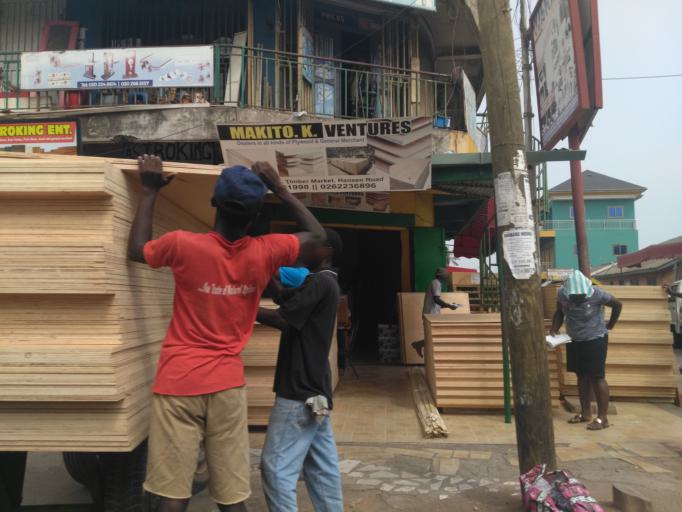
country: GH
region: Greater Accra
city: Accra
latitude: 5.5440
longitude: -0.2163
